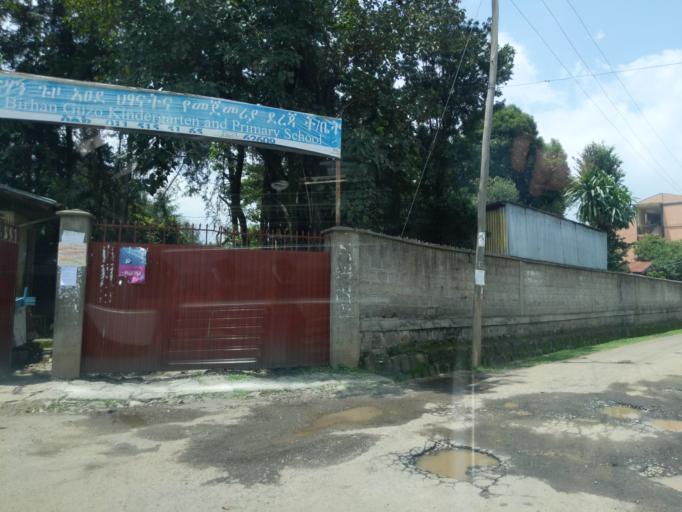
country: ET
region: Adis Abeba
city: Addis Ababa
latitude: 9.0189
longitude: 38.7781
